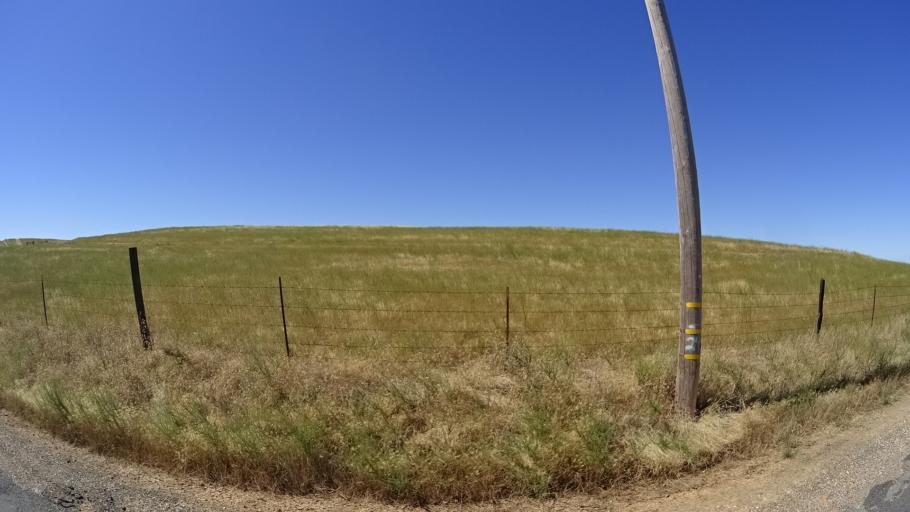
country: US
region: California
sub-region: Calaveras County
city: Rancho Calaveras
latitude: 38.0151
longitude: -120.8168
